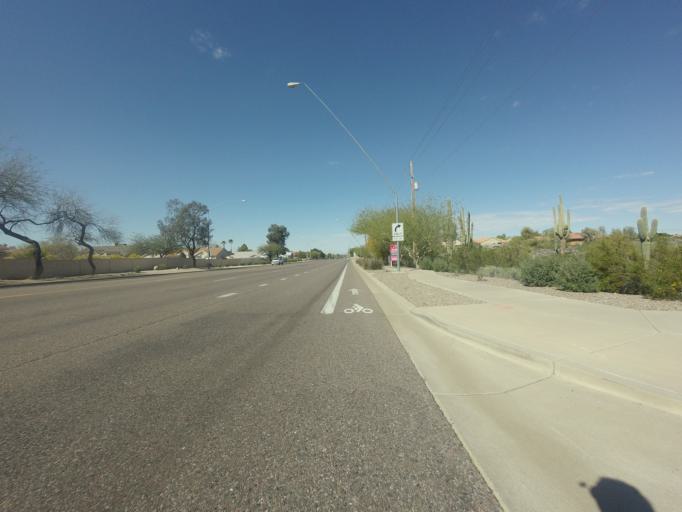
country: US
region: Arizona
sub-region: Maricopa County
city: Mesa
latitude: 33.4665
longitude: -111.6906
